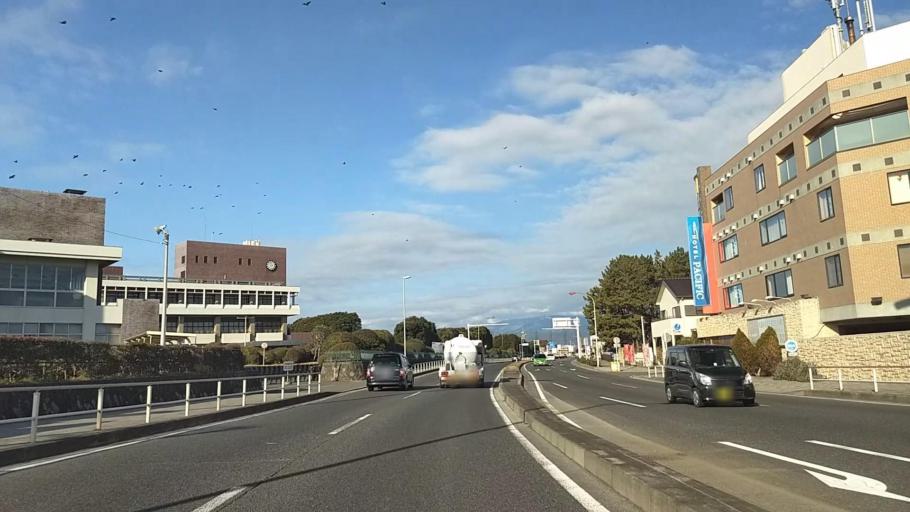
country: JP
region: Kanagawa
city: Chigasaki
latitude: 35.3175
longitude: 139.3818
